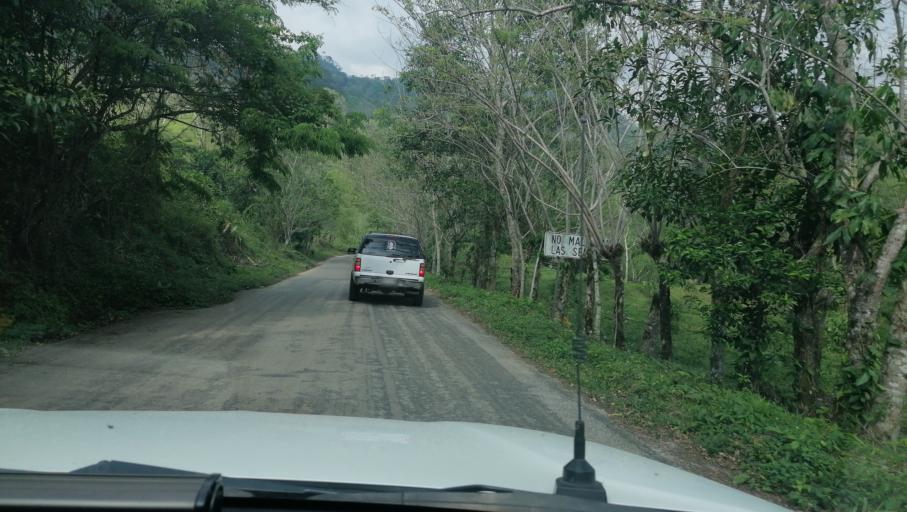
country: MX
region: Chiapas
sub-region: Francisco Leon
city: San Miguel la Sardina
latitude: 17.2246
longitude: -93.3447
